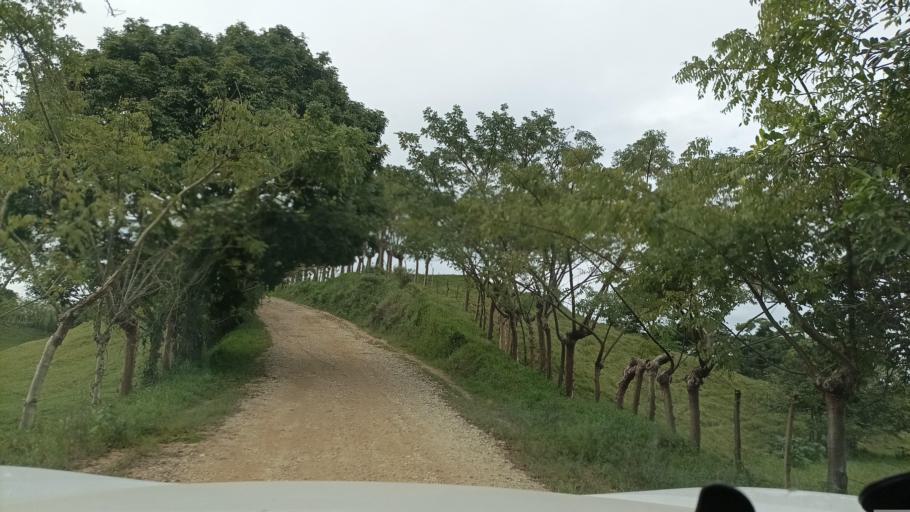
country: MX
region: Veracruz
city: Hidalgotitlan
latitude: 17.5977
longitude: -94.4213
